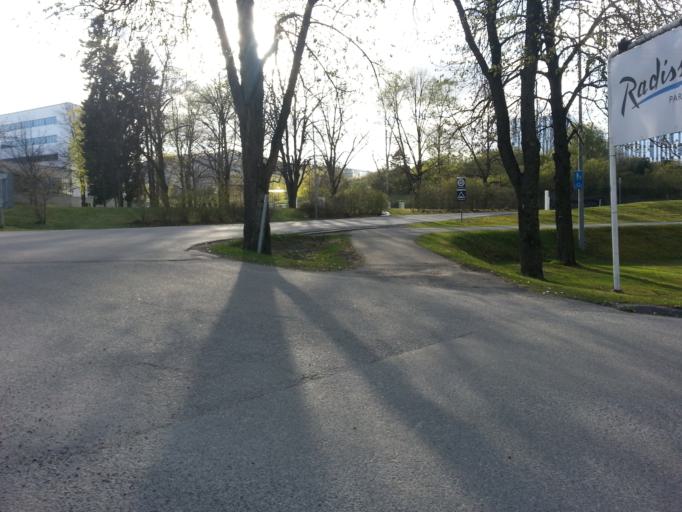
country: NO
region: Akershus
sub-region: Baerum
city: Lysaker
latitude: 59.9033
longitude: 10.6307
